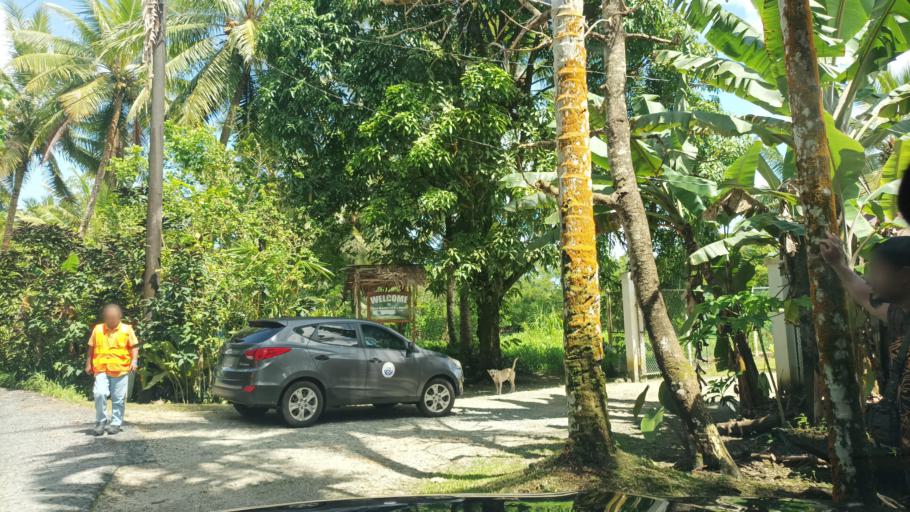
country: FM
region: Pohnpei
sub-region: Sokehs Municipality
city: Palikir - National Government Center
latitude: 6.9366
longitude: 158.1743
